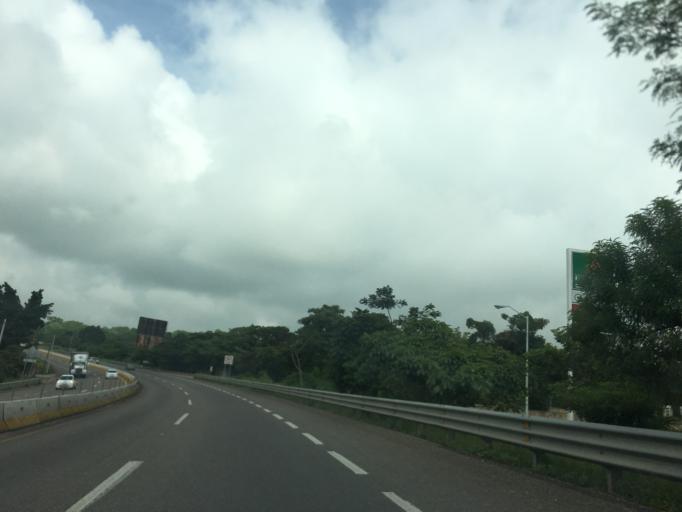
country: MX
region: Chiapas
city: Berriozabal
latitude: 16.7820
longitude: -93.2250
